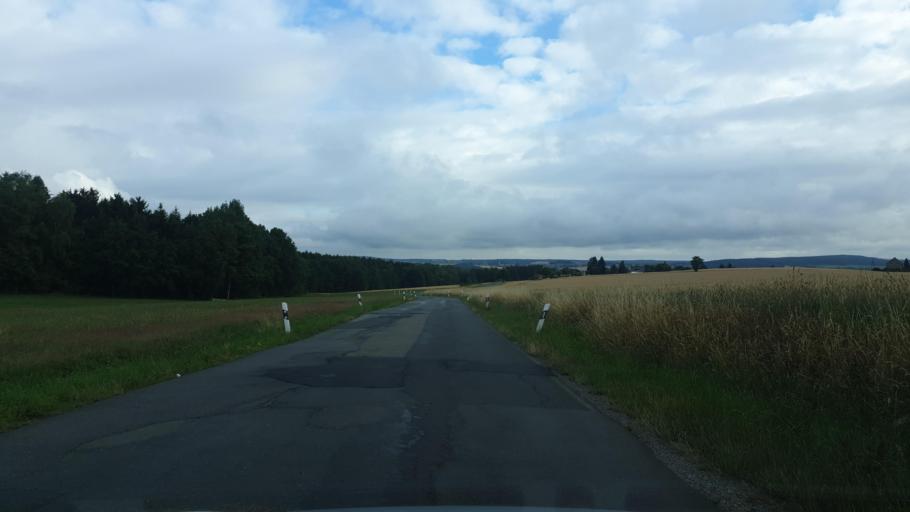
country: DE
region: Saxony
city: Limbach
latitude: 50.5946
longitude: 12.2407
